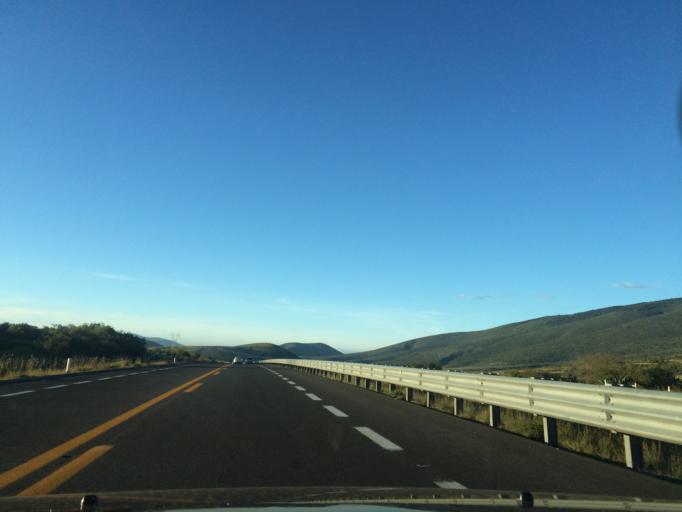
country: MX
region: Puebla
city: Morelos Canada
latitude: 18.7008
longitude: -97.4658
